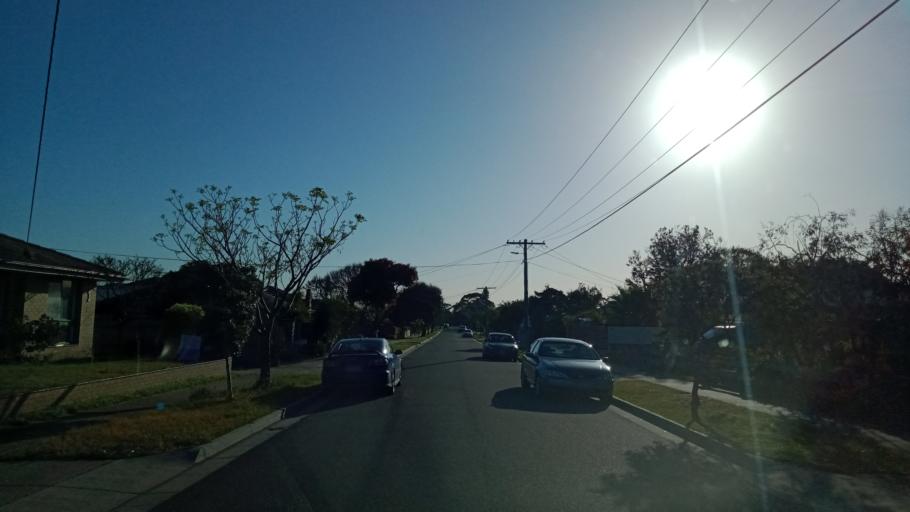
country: AU
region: Victoria
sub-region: Kingston
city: Chelsea
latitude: -38.0476
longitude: 145.1160
